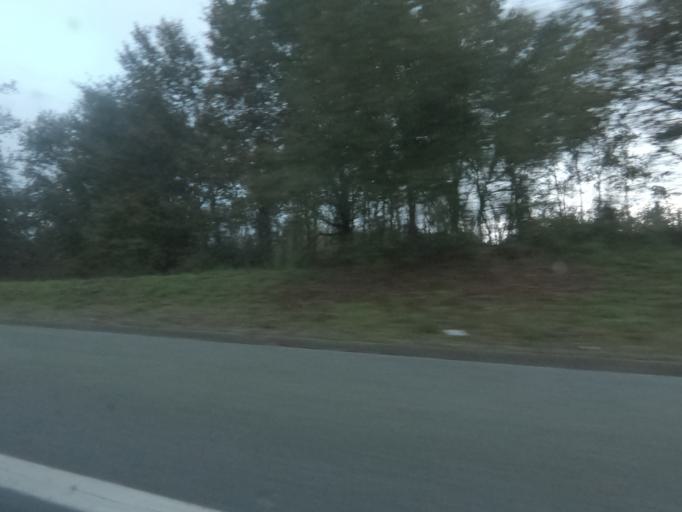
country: PT
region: Braga
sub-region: Vila Verde
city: Prado
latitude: 41.5457
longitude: -8.5016
